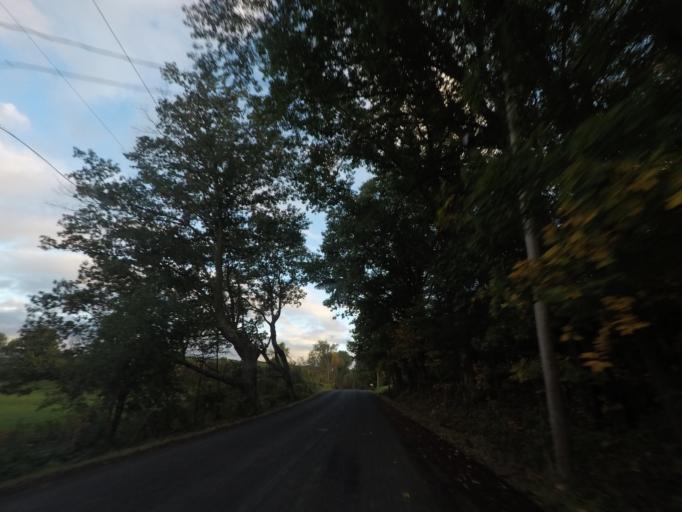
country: US
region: New York
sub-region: Rensselaer County
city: Nassau
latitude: 42.5218
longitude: -73.5908
